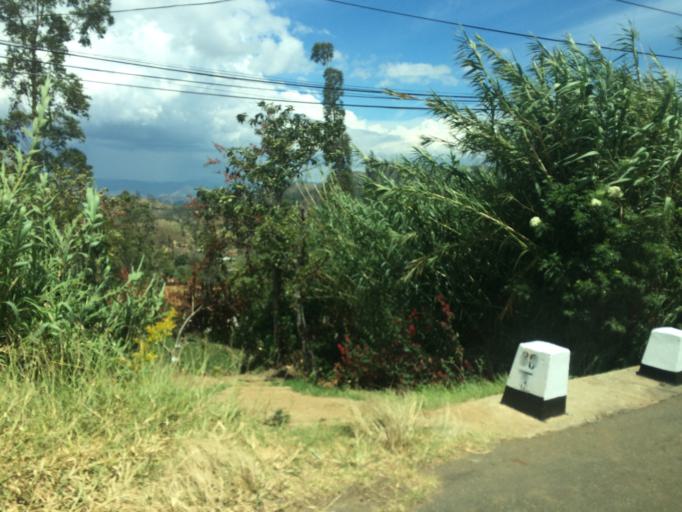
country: LK
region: Central
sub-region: Nuwara Eliya District
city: Nuwara Eliya
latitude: 6.9087
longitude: 80.8377
